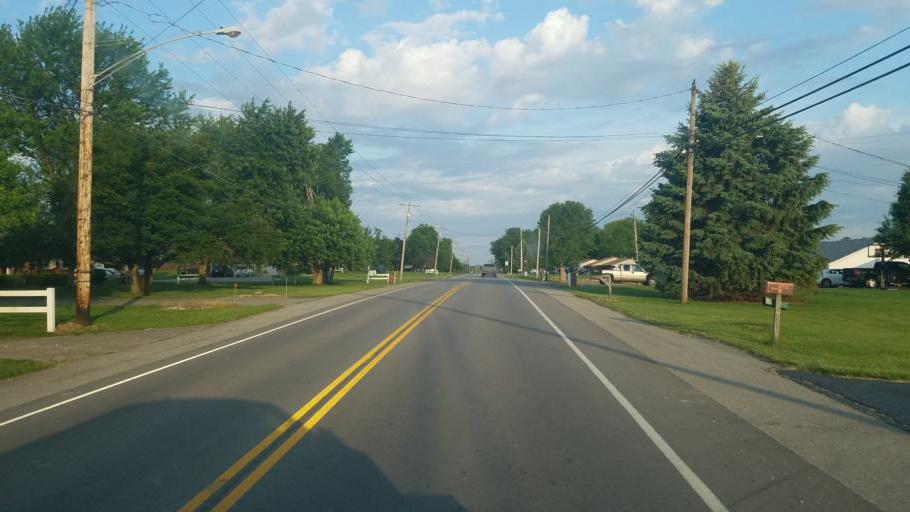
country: US
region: Ohio
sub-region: Highland County
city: Leesburg
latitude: 39.3462
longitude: -83.5652
